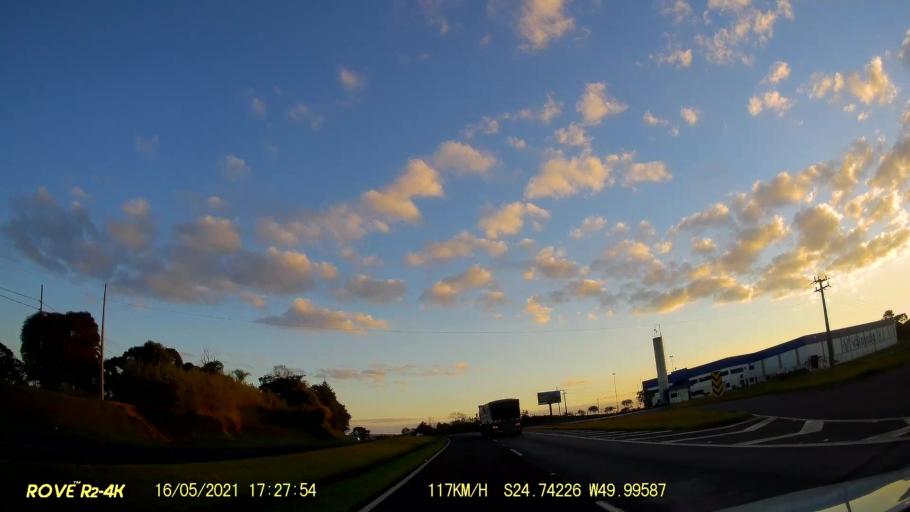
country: BR
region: Parana
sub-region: Castro
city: Castro
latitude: -24.7426
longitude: -49.9963
